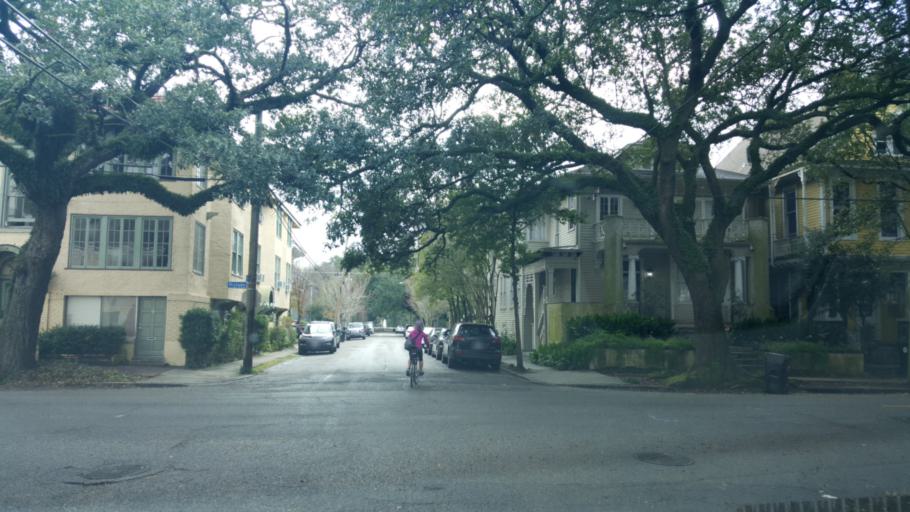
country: US
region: Louisiana
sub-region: Orleans Parish
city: New Orleans
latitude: 29.9363
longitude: -90.0759
